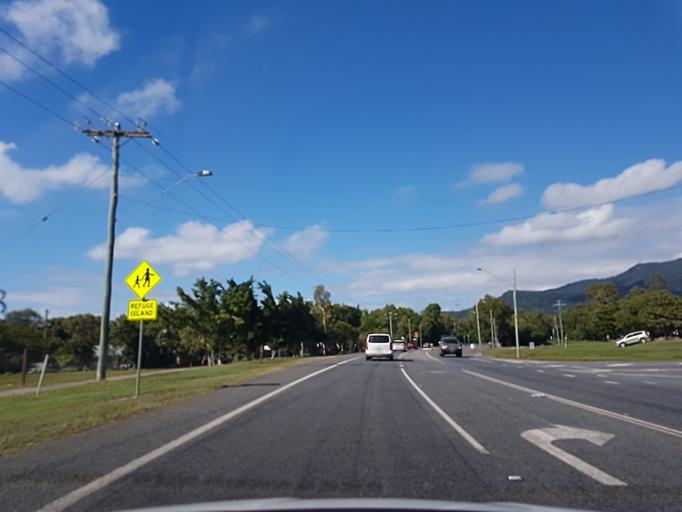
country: AU
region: Queensland
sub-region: Cairns
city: Palm Cove
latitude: -16.7742
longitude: 145.6751
